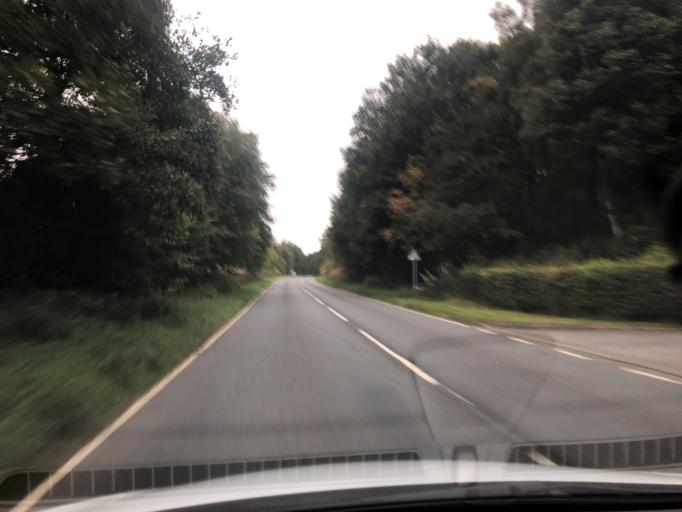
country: GB
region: Scotland
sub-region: Perth and Kinross
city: Pitlochry
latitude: 56.7491
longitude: -3.7930
